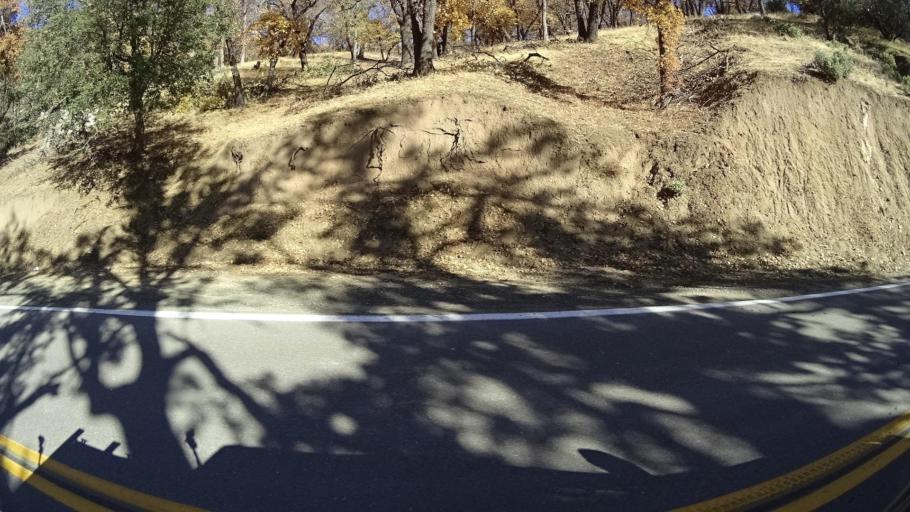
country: US
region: California
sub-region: Kern County
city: Alta Sierra
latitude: 35.7426
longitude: -118.6063
